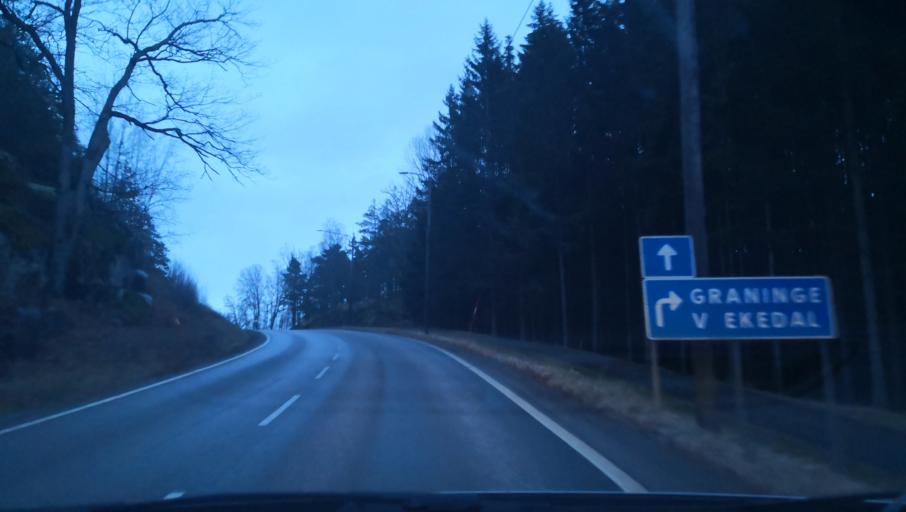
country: SE
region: Stockholm
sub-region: Varmdo Kommun
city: Gustavsberg
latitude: 59.3288
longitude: 18.3534
